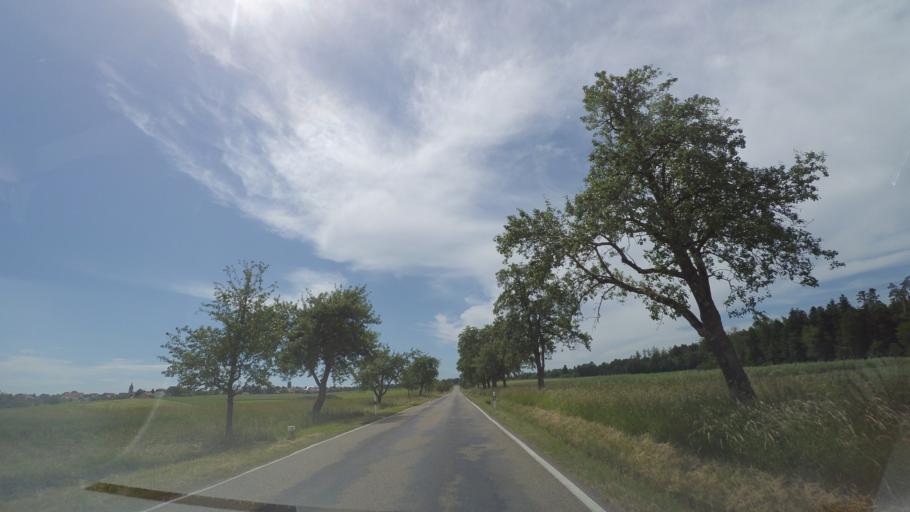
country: DE
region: Baden-Wuerttemberg
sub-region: Regierungsbezirk Stuttgart
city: Kaisersbach
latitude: 48.9359
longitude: 9.6514
